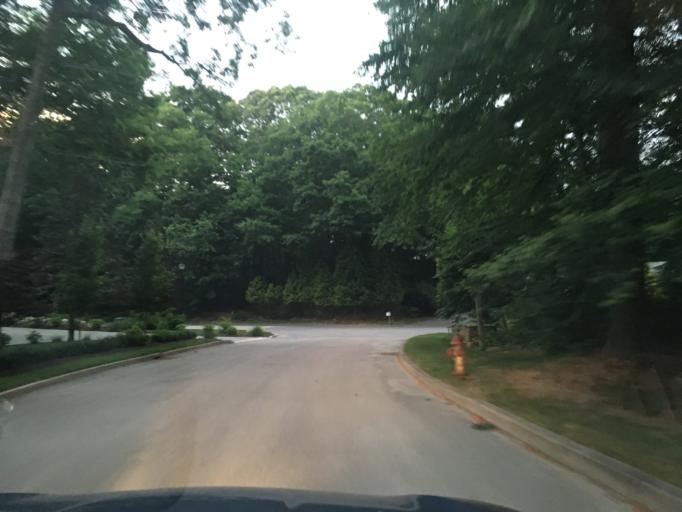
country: US
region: Rhode Island
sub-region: Washington County
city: Exeter
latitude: 41.6277
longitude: -71.5163
